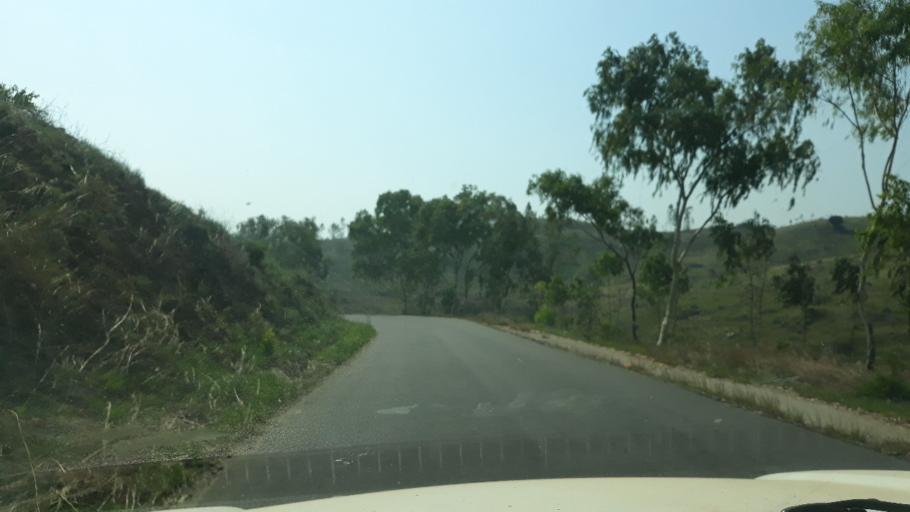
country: CD
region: South Kivu
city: Uvira
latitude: -3.2019
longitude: 29.1596
